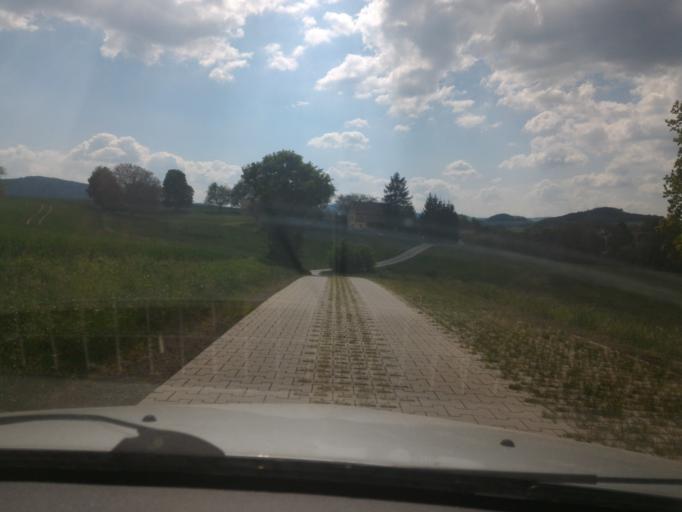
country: DE
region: Saxony
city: Bertsdorf-Hoernitz
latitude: 50.8908
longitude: 14.7497
